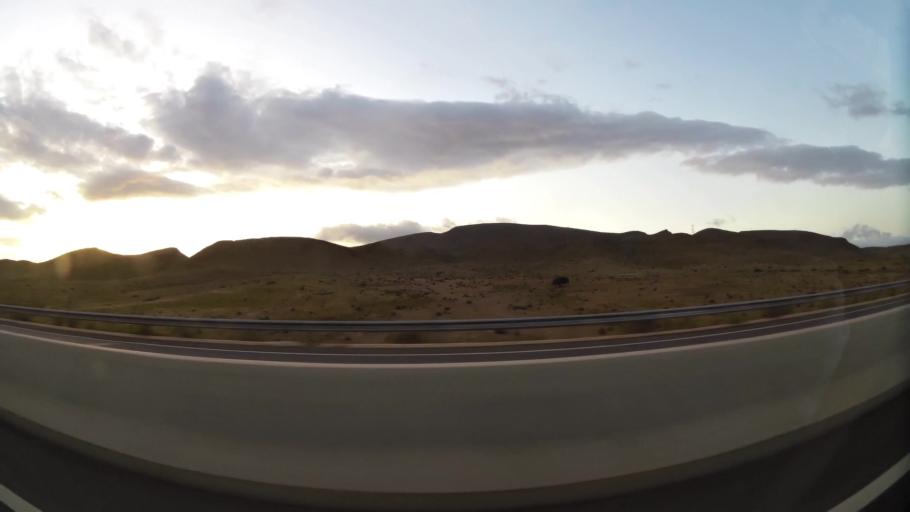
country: MA
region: Oriental
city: El Aioun
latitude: 34.5993
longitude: -2.6388
